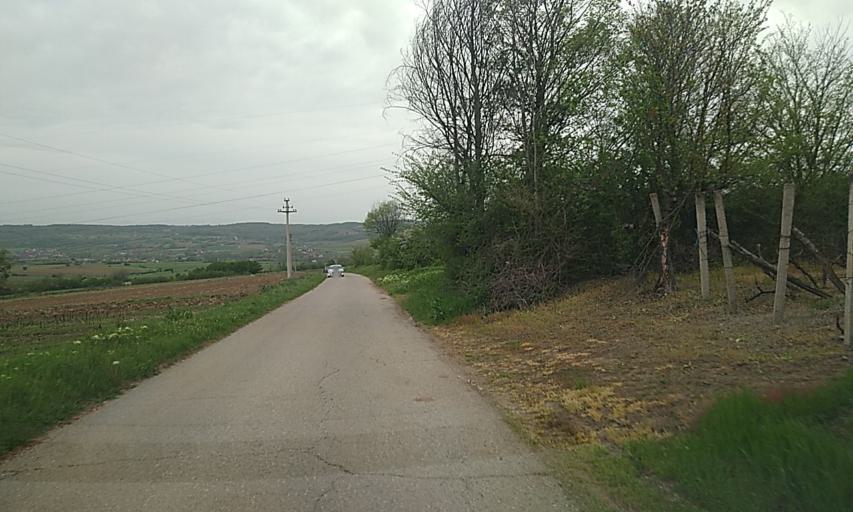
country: RS
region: Central Serbia
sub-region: Nisavski Okrug
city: Razanj
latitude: 43.5725
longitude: 21.5249
